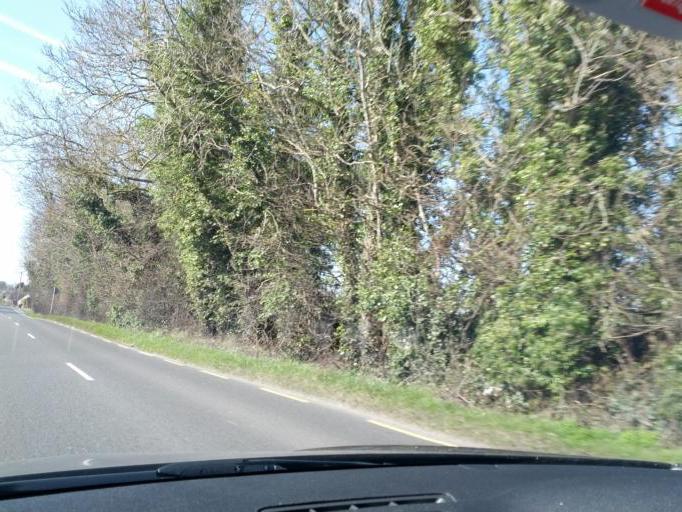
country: IE
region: Leinster
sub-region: Kildare
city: Leixlip
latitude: 53.3463
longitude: -6.4973
